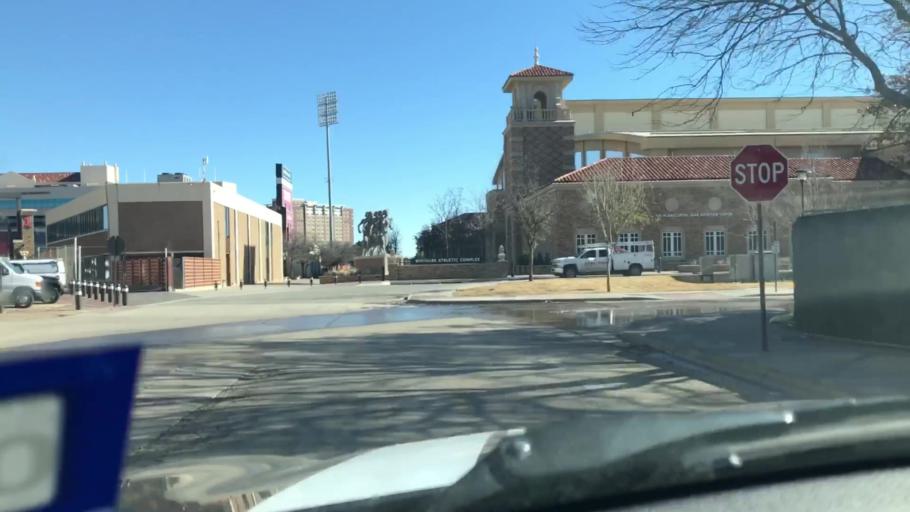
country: US
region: Texas
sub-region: Lubbock County
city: Lubbock
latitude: 33.5901
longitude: -101.8745
